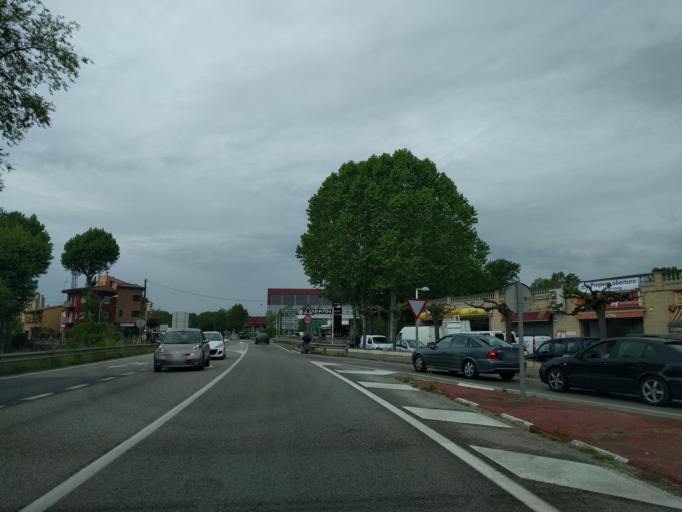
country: ES
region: Catalonia
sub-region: Provincia de Girona
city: Breda
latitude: 41.7195
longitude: 2.5482
